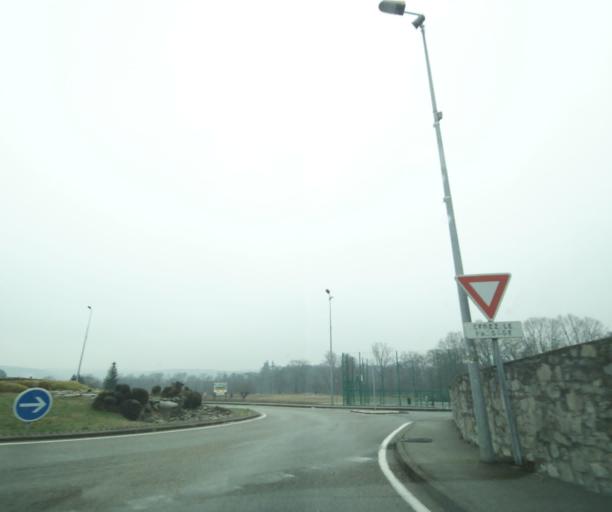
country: FR
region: Rhone-Alpes
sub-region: Departement de l'Ardeche
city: Aubenas
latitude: 44.6264
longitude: 4.3987
